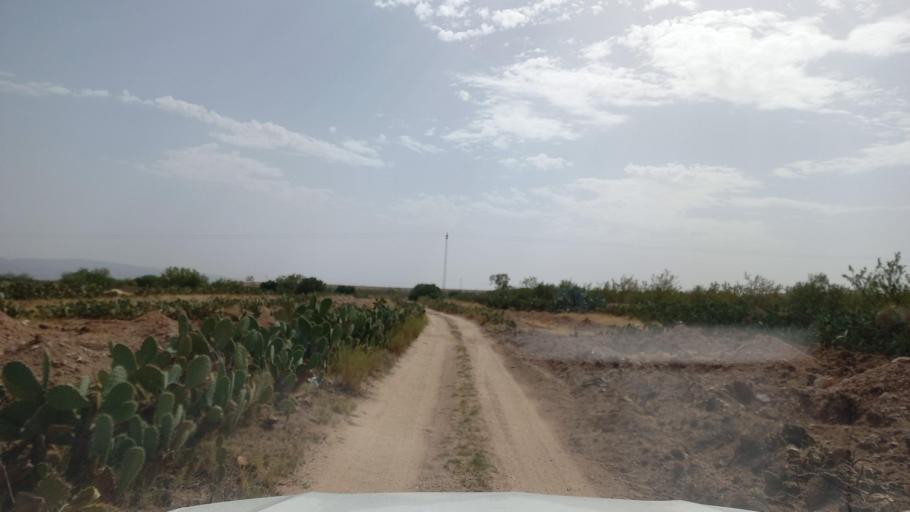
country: TN
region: Al Qasrayn
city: Kasserine
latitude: 35.2961
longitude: 8.9474
